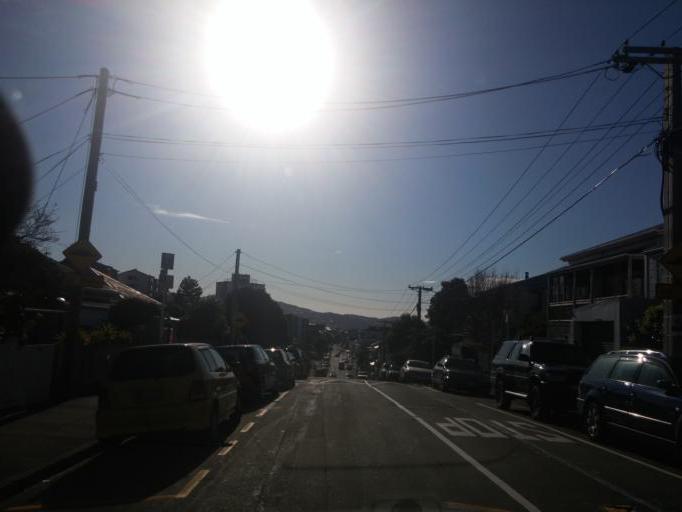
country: NZ
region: Wellington
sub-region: Wellington City
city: Wellington
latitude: -41.3103
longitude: 174.7758
